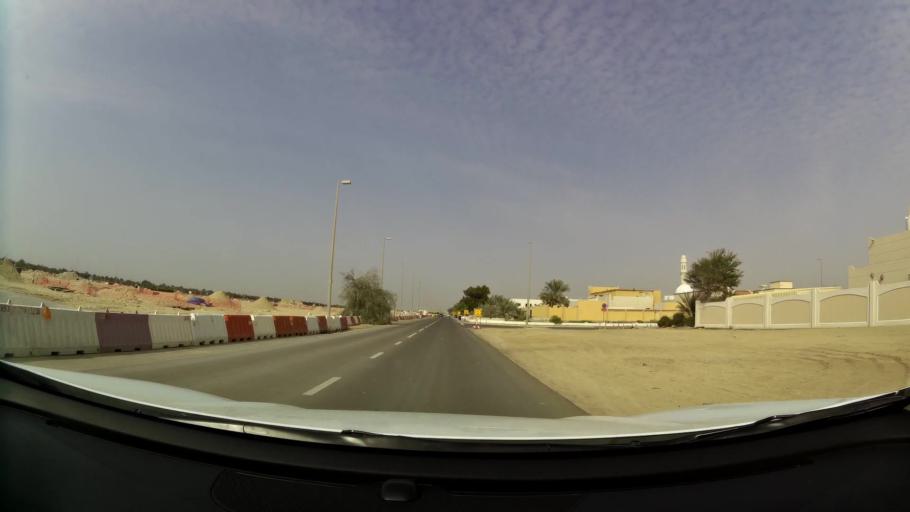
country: AE
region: Abu Dhabi
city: Abu Dhabi
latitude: 24.6026
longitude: 54.6977
